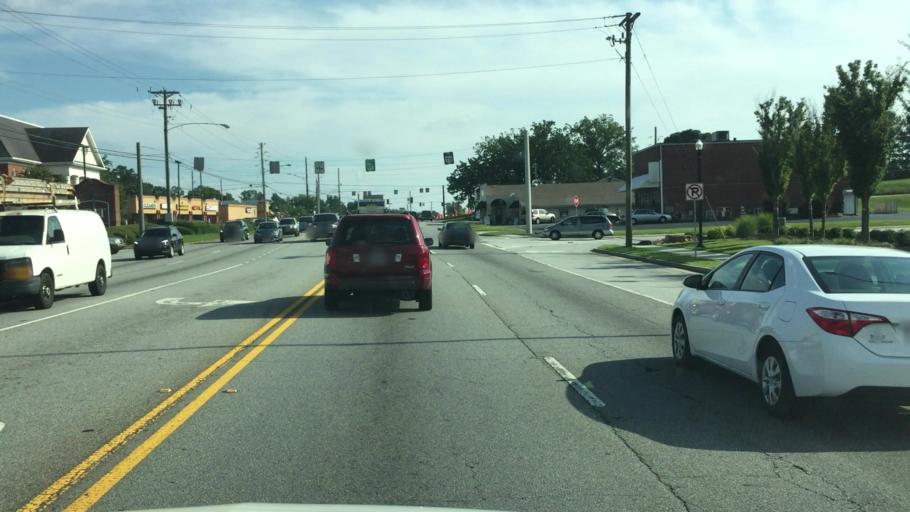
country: US
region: Georgia
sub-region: Gwinnett County
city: Snellville
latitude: 33.8601
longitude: -84.0190
